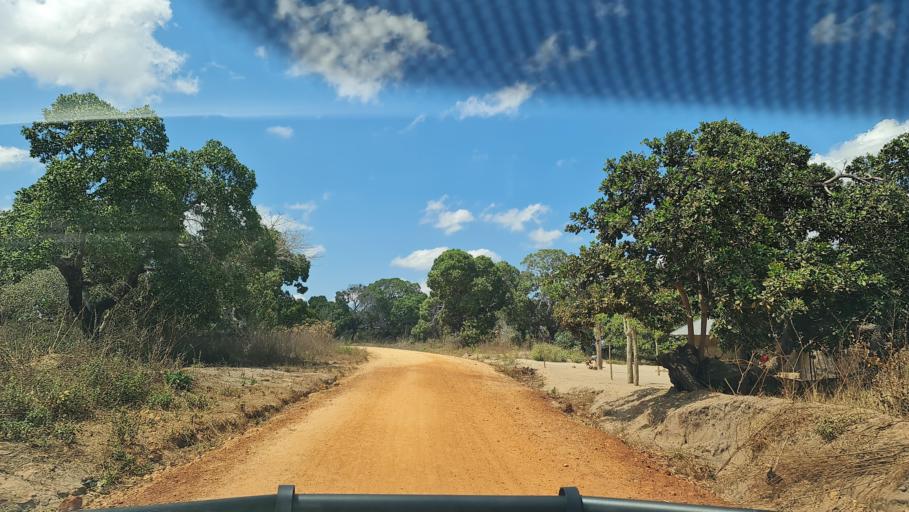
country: MZ
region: Nampula
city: Nacala
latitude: -14.1702
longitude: 40.2572
